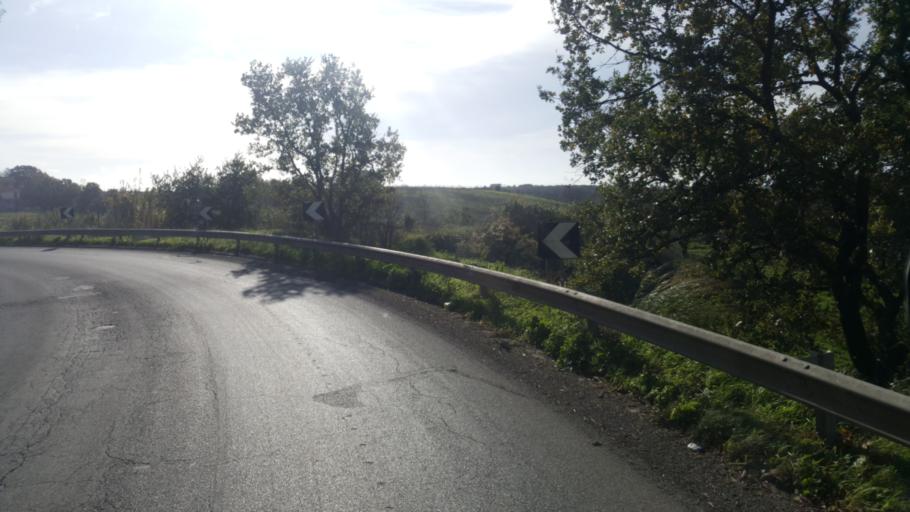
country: IT
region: Latium
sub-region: Citta metropolitana di Roma Capitale
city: Mantiglia di Ardea
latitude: 41.6518
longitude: 12.6217
